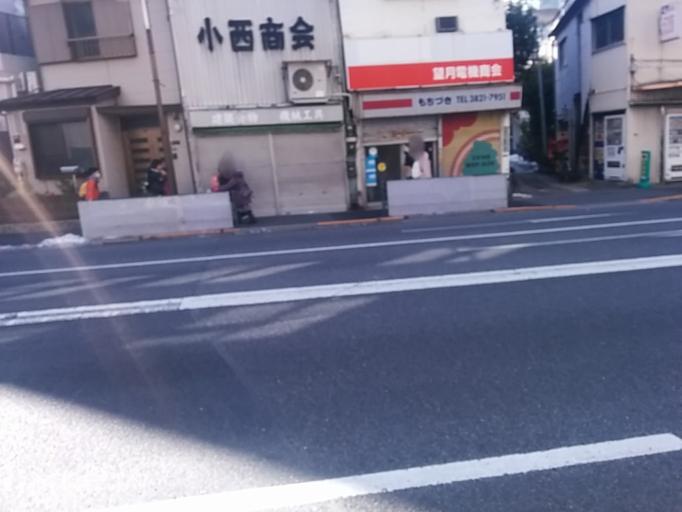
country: JP
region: Tokyo
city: Tokyo
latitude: 35.7290
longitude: 139.7631
